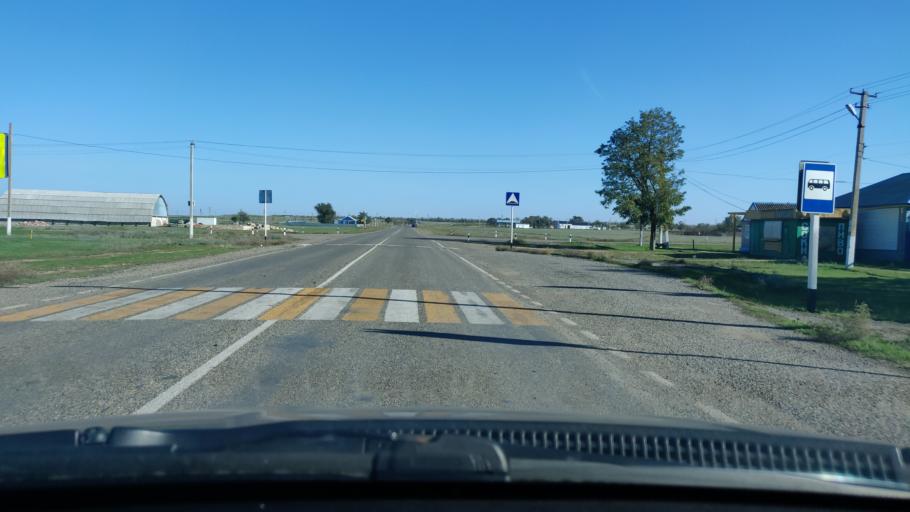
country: RU
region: Stavropol'skiy
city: Letnyaya Stavka
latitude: 45.3747
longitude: 43.6857
